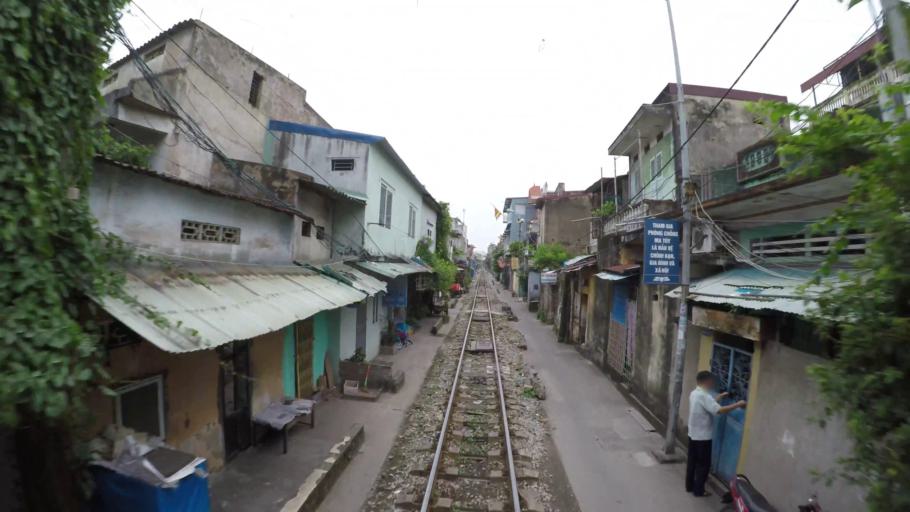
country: VN
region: Hai Phong
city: Haiphong
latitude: 20.8583
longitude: 106.6642
